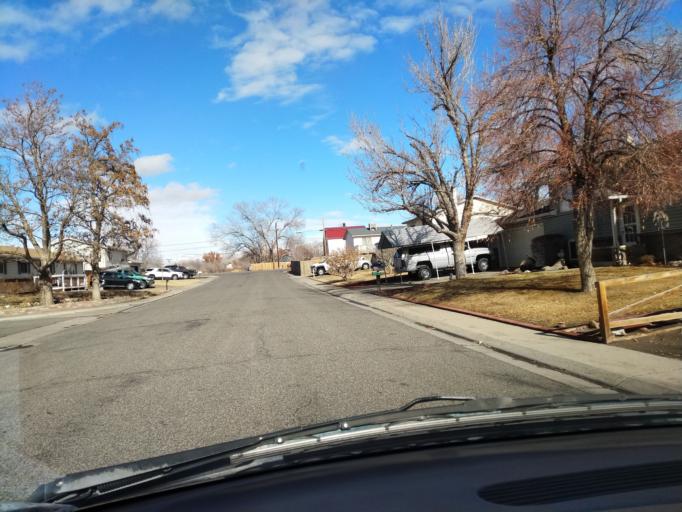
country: US
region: Colorado
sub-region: Mesa County
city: Fruitvale
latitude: 39.0764
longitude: -108.4878
